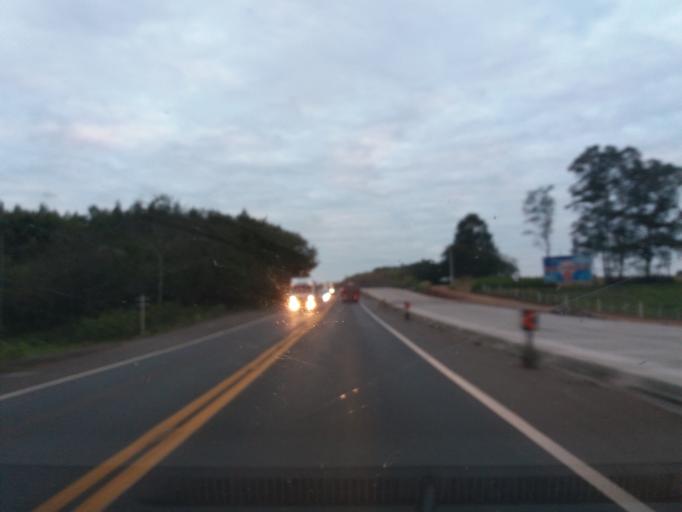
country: BR
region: Parana
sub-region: Realeza
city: Realeza
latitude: -25.3978
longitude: -53.5765
